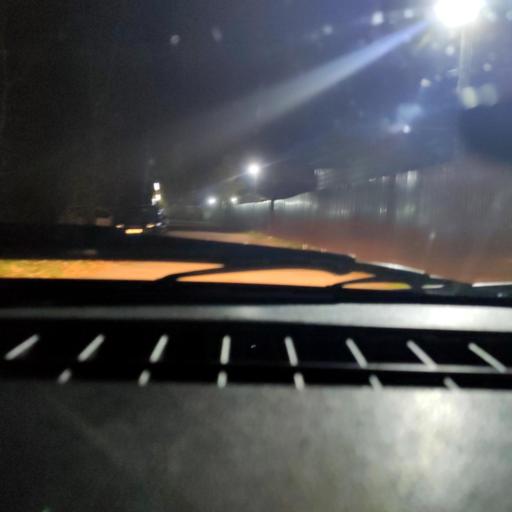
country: RU
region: Bashkortostan
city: Ufa
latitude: 54.7842
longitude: 56.1008
